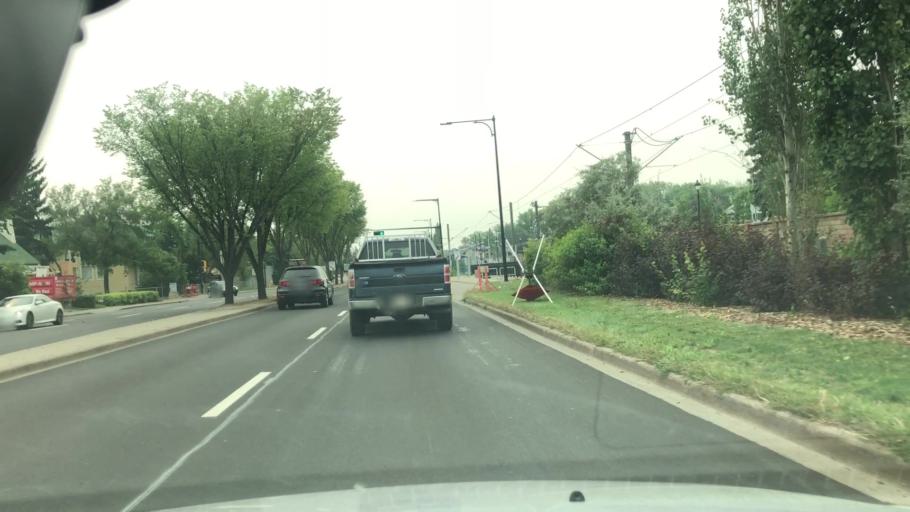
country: CA
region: Alberta
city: Edmonton
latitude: 53.5150
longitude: -113.5260
